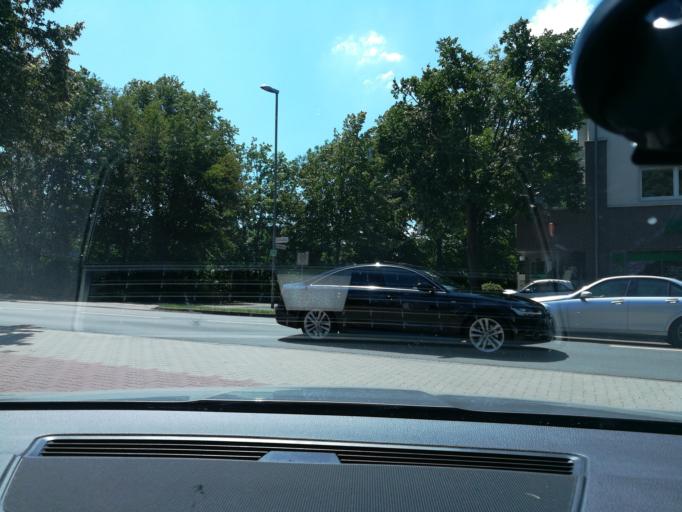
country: DE
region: North Rhine-Westphalia
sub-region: Regierungsbezirk Detmold
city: Minden
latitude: 52.3022
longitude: 8.9072
